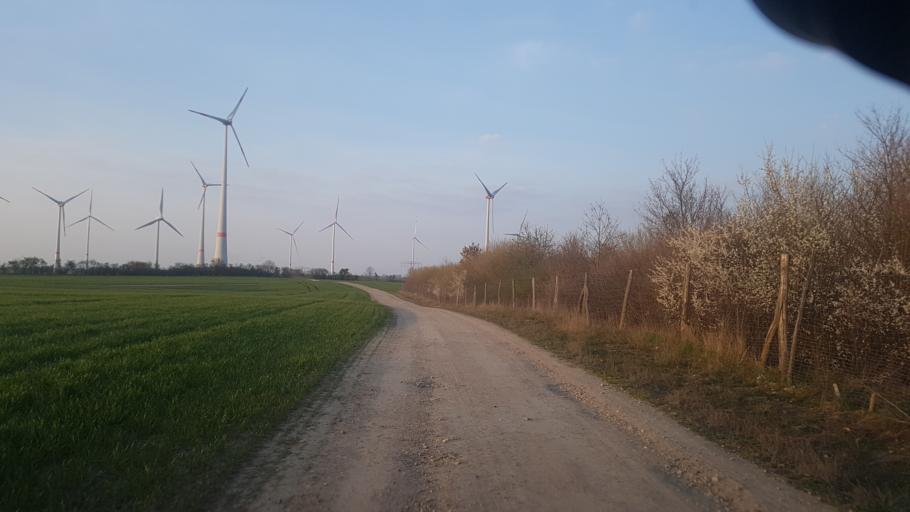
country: DE
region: Brandenburg
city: Gramzow
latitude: 53.2110
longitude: 13.9542
